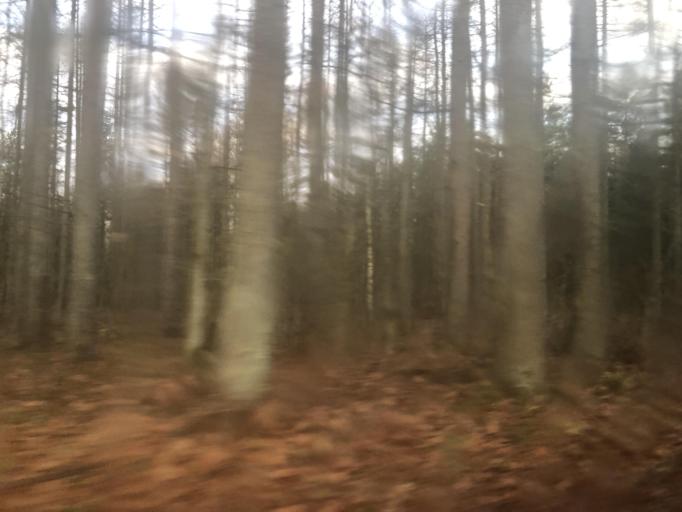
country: SE
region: Skane
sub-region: Lunds Kommun
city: Veberod
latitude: 55.6083
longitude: 13.5387
